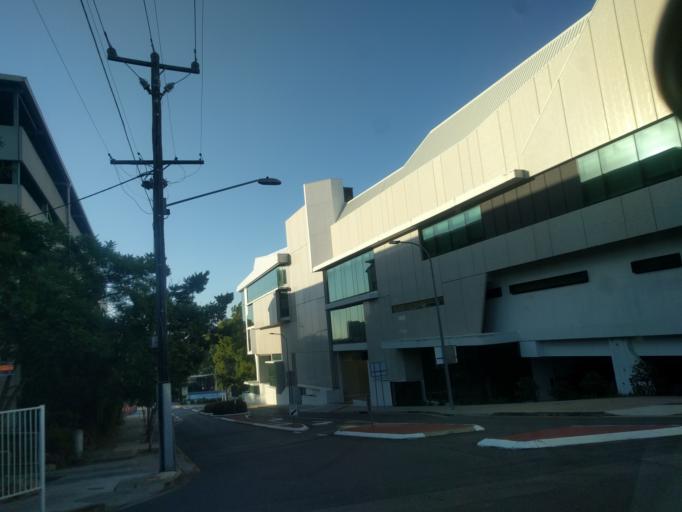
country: AU
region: Queensland
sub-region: Brisbane
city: Fortitude Valley
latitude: -27.4482
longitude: 153.0248
